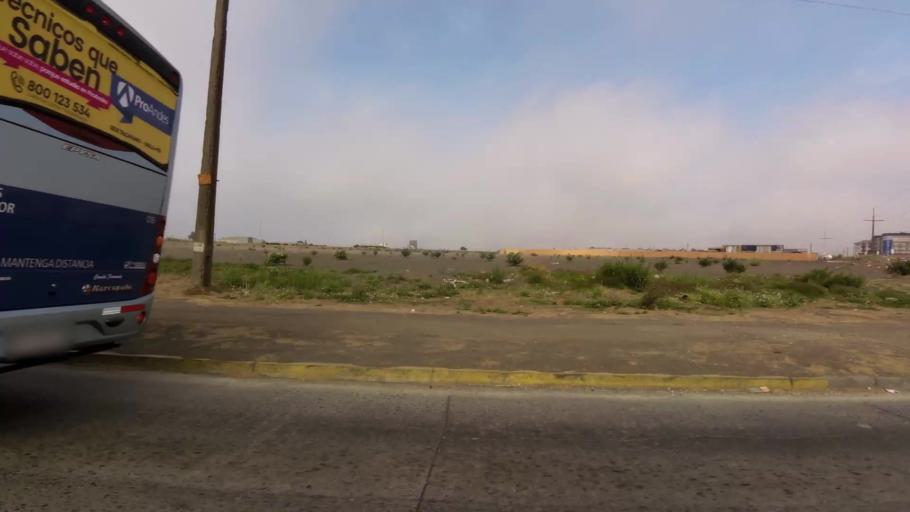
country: CL
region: Biobio
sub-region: Provincia de Concepcion
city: Concepcion
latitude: -36.8008
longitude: -73.1059
